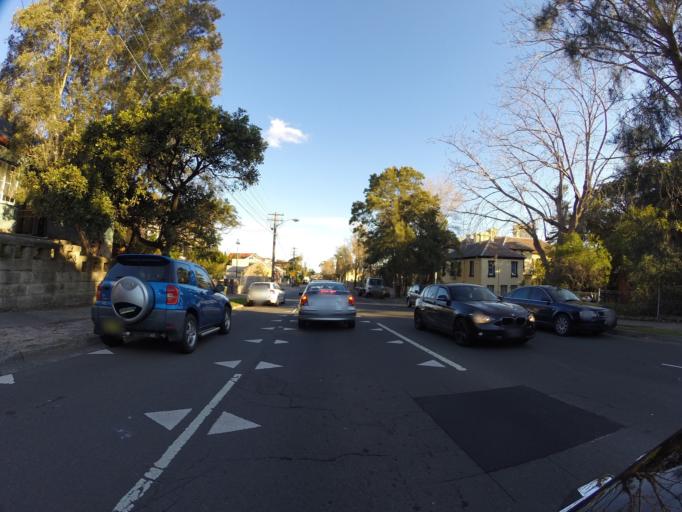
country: AU
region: New South Wales
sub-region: Waverley
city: Bondi Junction
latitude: -33.8970
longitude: 151.2543
